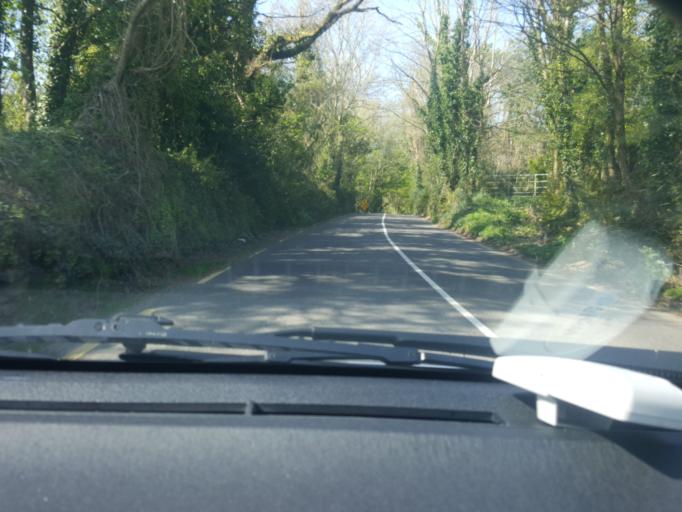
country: IE
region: Munster
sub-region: County Cork
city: Bandon
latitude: 51.7603
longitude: -8.6476
